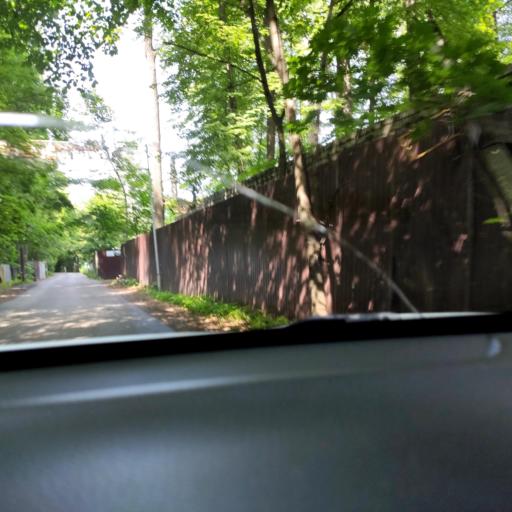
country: RU
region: Tatarstan
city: Verkhniy Uslon
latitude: 55.6551
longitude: 49.0277
